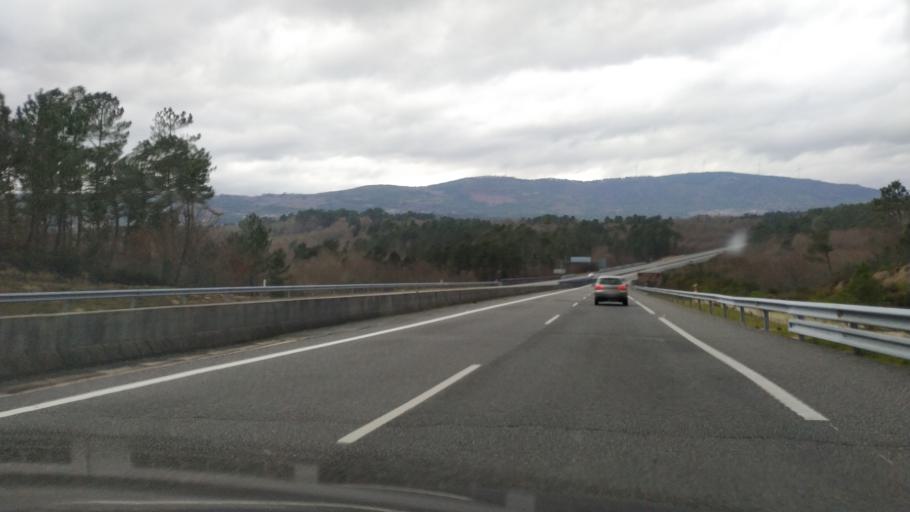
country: ES
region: Galicia
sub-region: Provincia de Ourense
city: Cea
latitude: 42.4607
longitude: -8.0243
